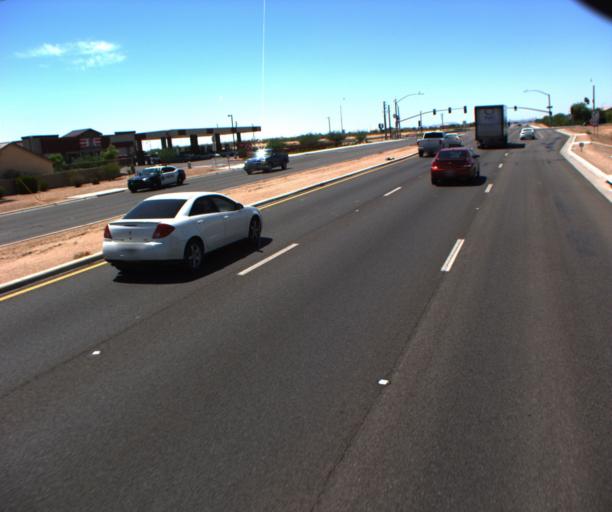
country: US
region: Arizona
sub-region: Pinal County
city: Maricopa
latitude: 33.0453
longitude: -112.0481
